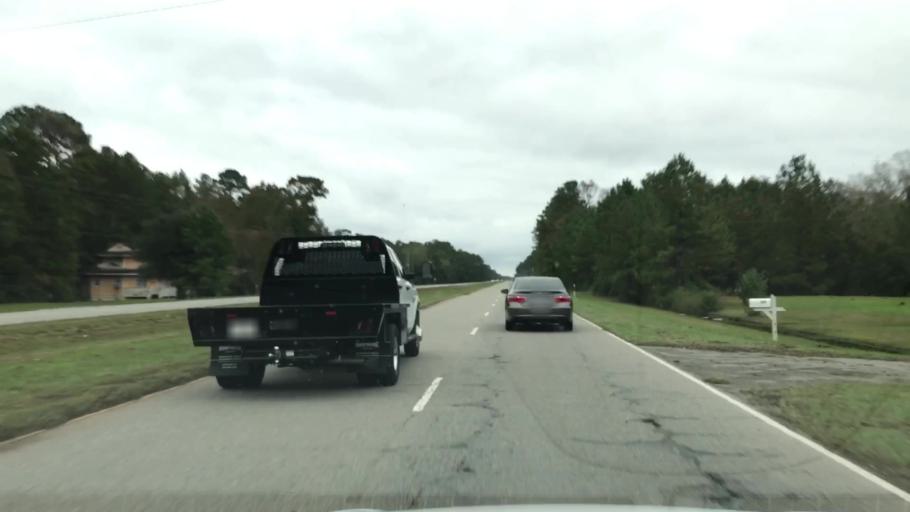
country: US
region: South Carolina
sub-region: Georgetown County
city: Georgetown
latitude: 33.3020
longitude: -79.3395
